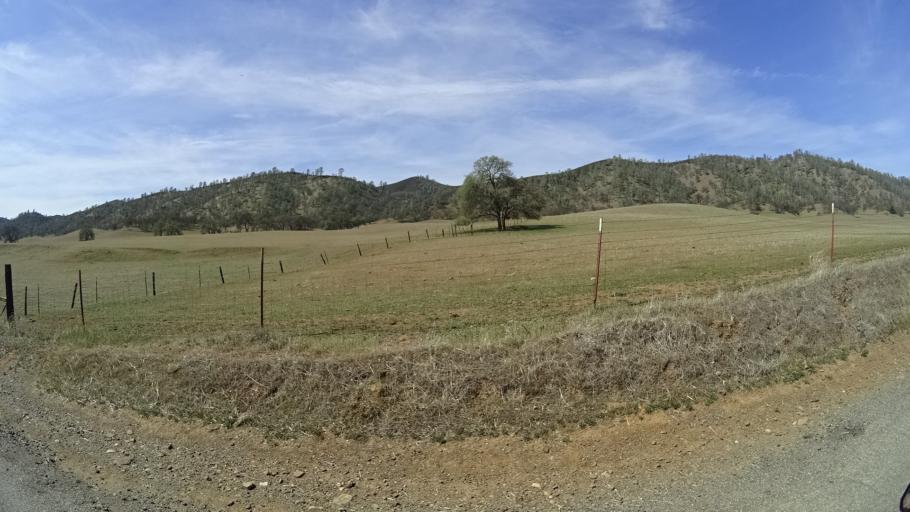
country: US
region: California
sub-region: Glenn County
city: Willows
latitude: 39.4762
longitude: -122.4490
